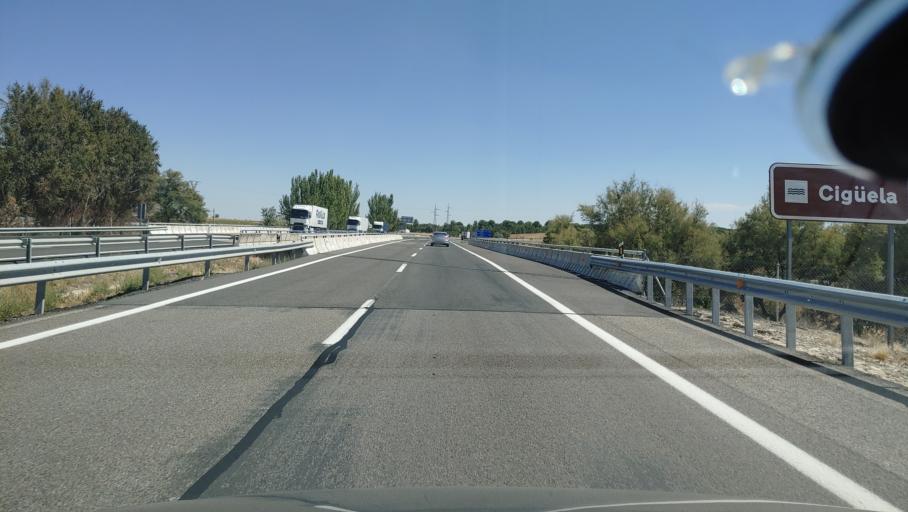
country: ES
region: Castille-La Mancha
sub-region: Provincia de Ciudad Real
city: Villarta de San Juan
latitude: 39.2456
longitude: -3.4230
